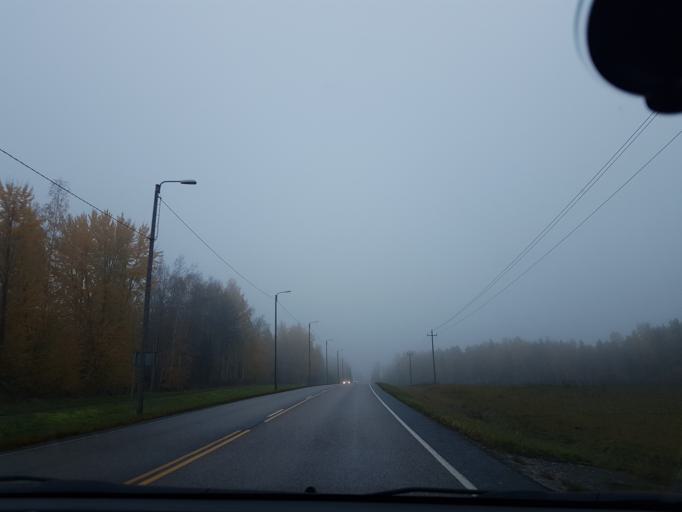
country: FI
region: Uusimaa
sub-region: Helsinki
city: Tuusula
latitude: 60.4325
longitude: 25.0591
